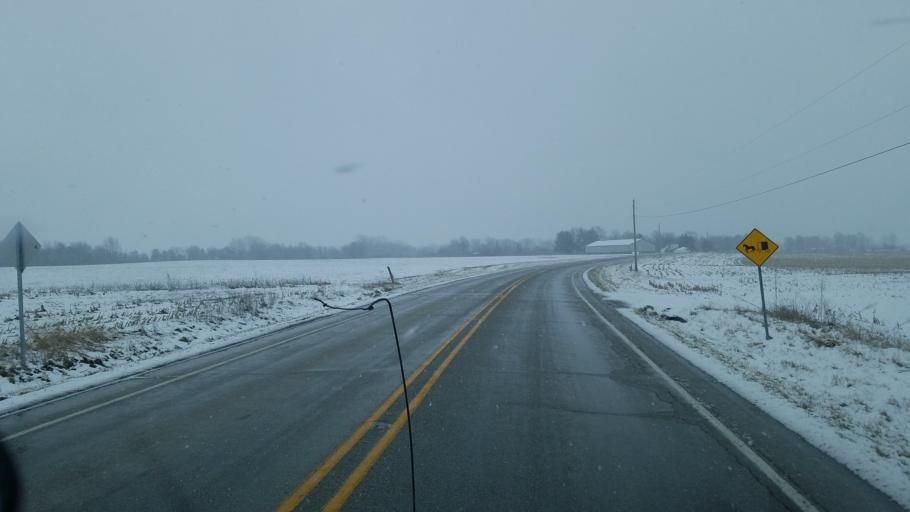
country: US
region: Indiana
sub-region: Randolph County
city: Lynn
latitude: 39.9385
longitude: -84.9784
